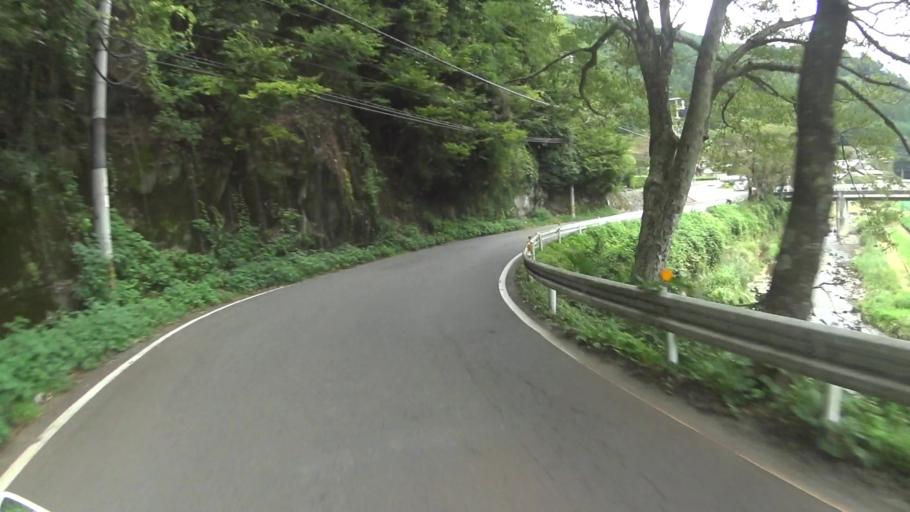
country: JP
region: Kyoto
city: Uji
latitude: 34.8270
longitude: 135.9386
